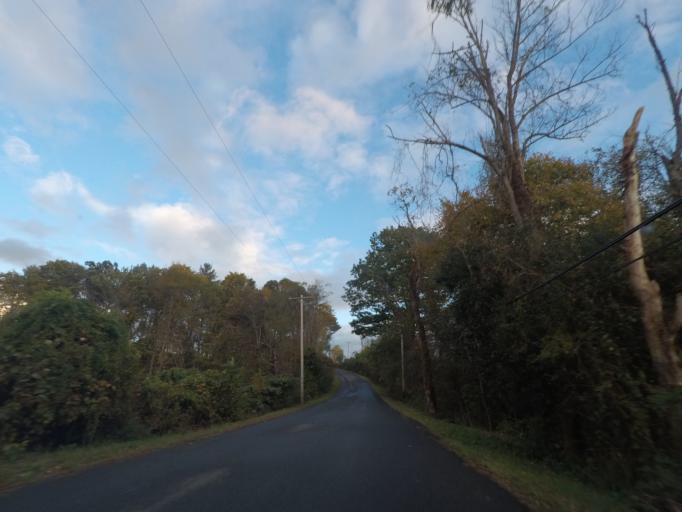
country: US
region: New York
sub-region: Rensselaer County
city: Nassau
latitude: 42.5504
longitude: -73.5888
